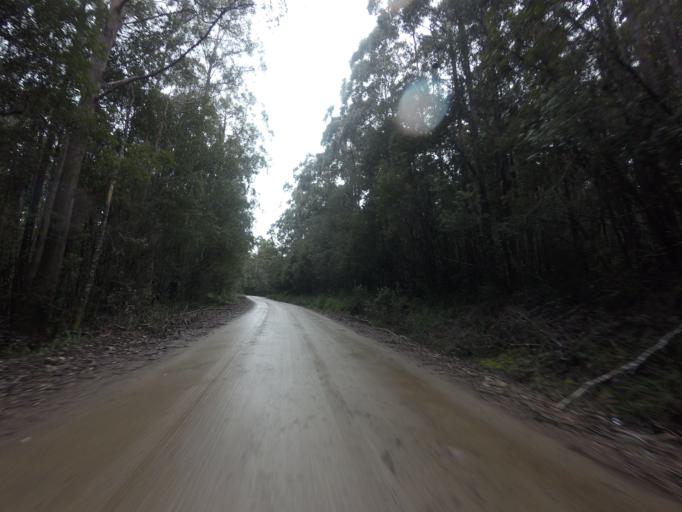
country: AU
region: Tasmania
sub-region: Huon Valley
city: Geeveston
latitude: -43.4943
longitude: 146.8808
